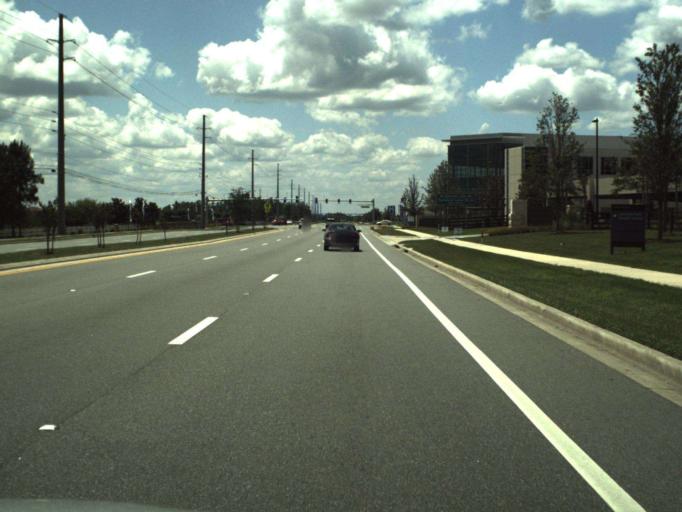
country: US
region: Florida
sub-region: Osceola County
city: Buenaventura Lakes
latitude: 28.3751
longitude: -81.2446
